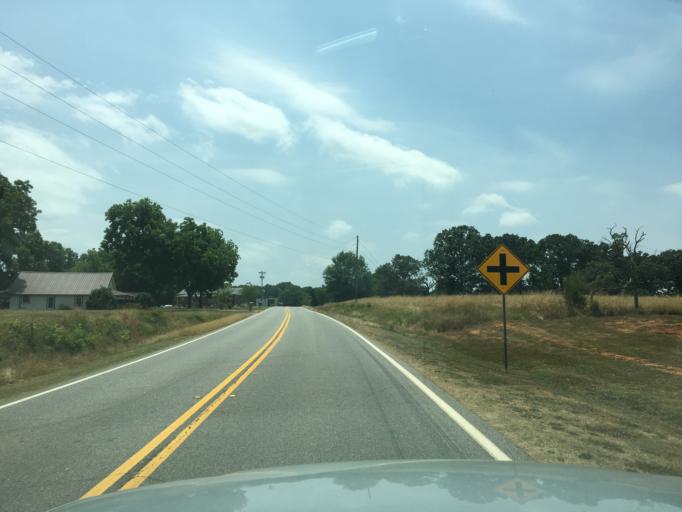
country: US
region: Georgia
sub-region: Madison County
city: Danielsville
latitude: 34.2191
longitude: -83.2263
